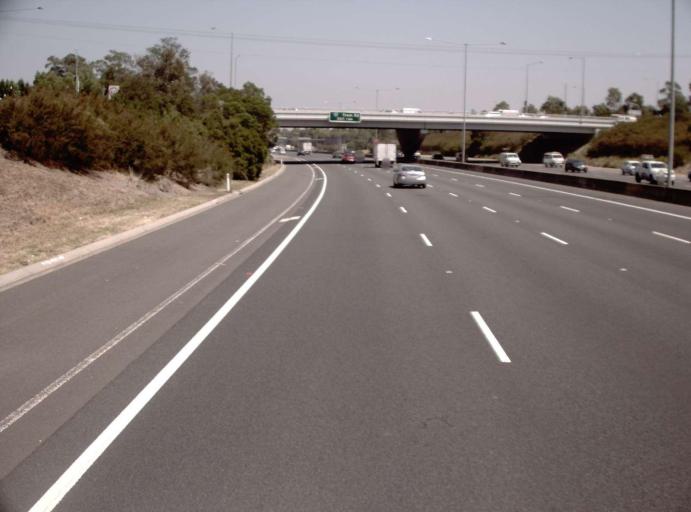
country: AU
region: Victoria
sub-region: Manningham
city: Doncaster East
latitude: -37.7987
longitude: 145.1438
